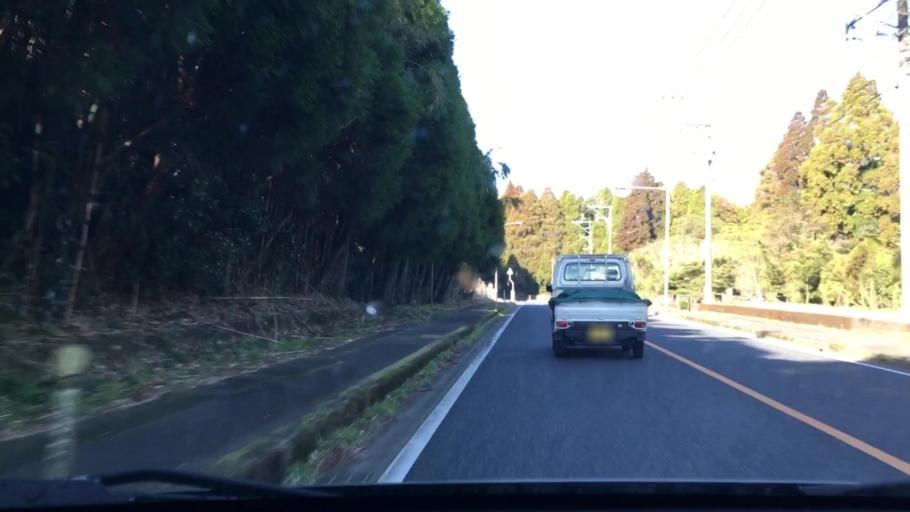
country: JP
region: Kagoshima
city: Kokubu-matsuki
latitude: 31.6719
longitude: 130.8626
